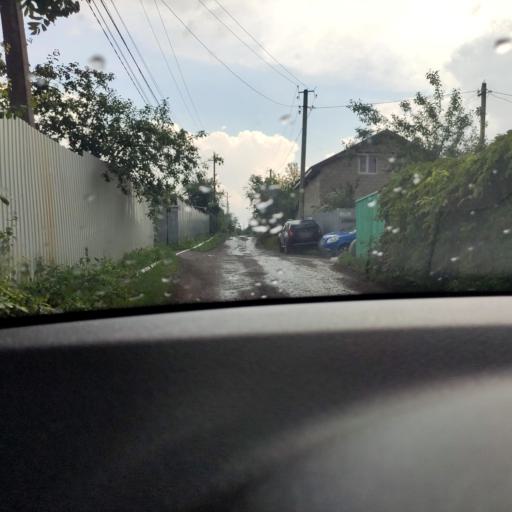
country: RU
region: Samara
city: Novosemeykino
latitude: 53.4007
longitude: 50.3142
